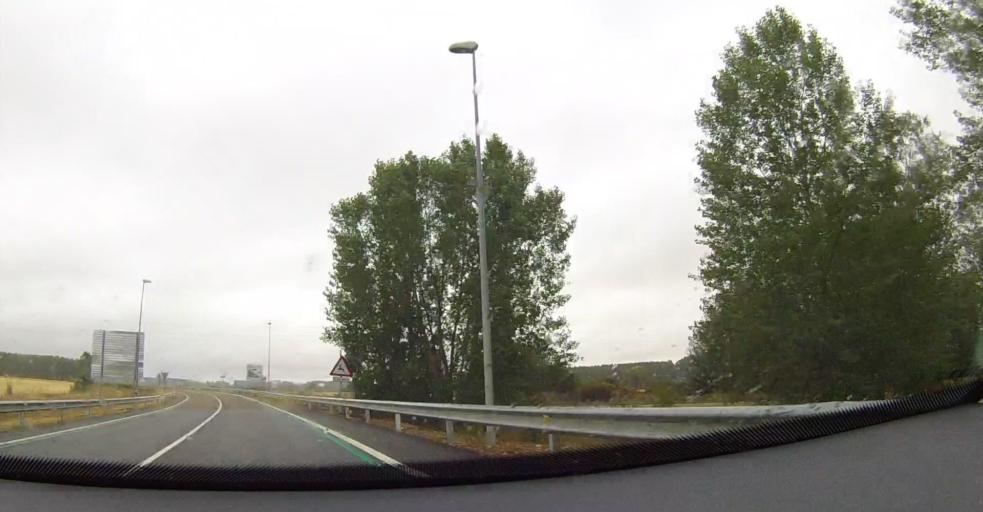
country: ES
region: Castille and Leon
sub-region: Provincia de Palencia
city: Carrion de los Condes
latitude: 42.3512
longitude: -4.6239
